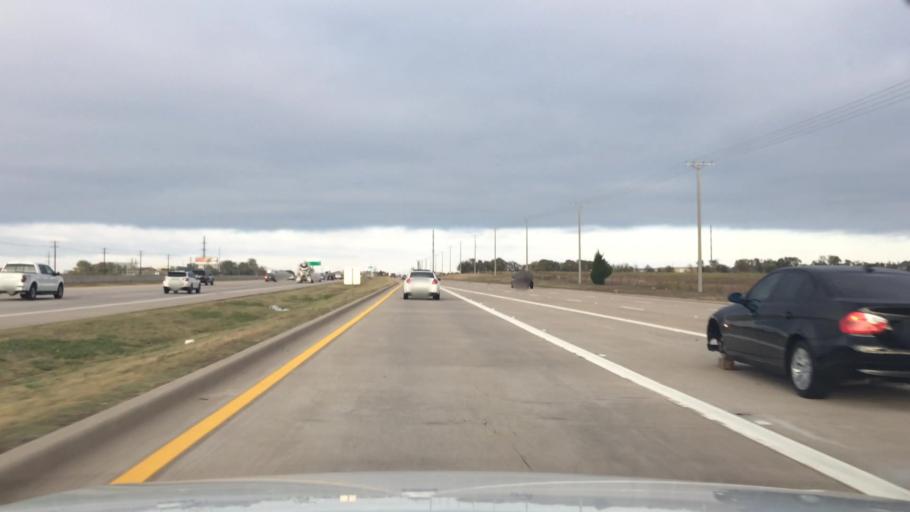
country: US
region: Texas
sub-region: Collin County
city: Frisco
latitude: 33.1065
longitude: -96.7815
